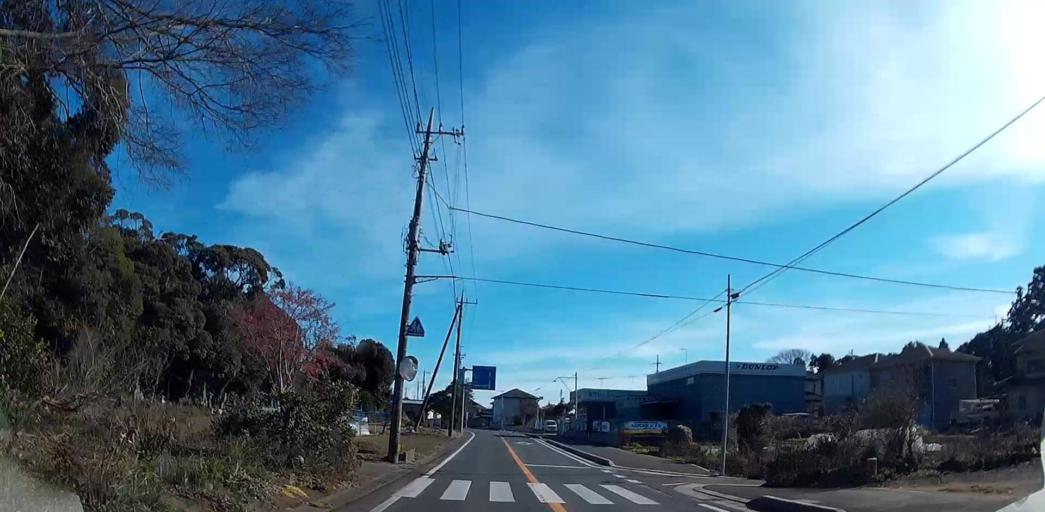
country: JP
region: Chiba
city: Yokaichiba
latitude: 35.7371
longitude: 140.4876
